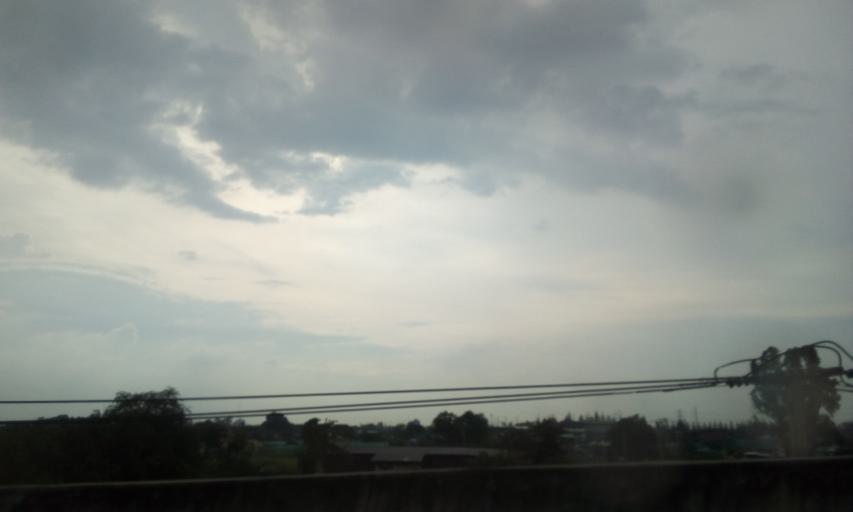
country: TH
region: Phra Nakhon Si Ayutthaya
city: Ban Bang Kadi Pathum Thani
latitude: 13.9661
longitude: 100.5504
